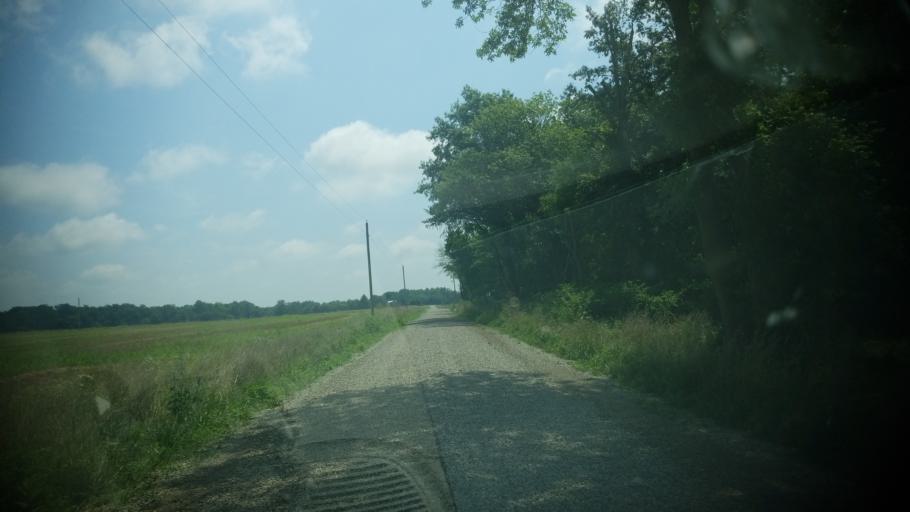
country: US
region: Illinois
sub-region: Wayne County
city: Fairfield
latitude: 38.5297
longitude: -88.3724
